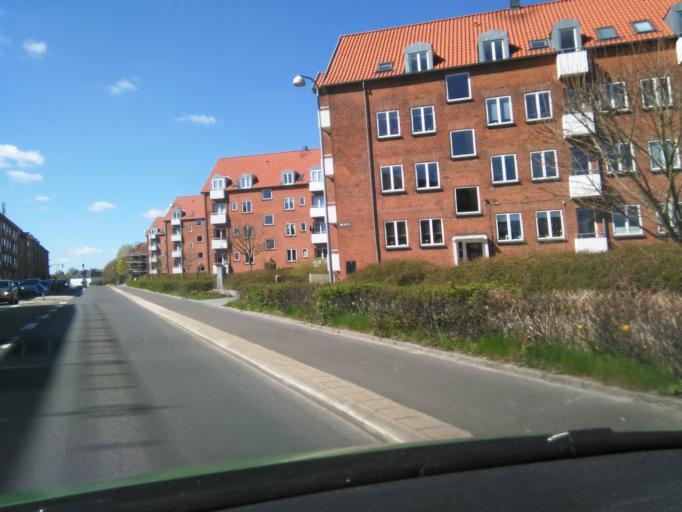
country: DK
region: Central Jutland
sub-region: Horsens Kommune
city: Horsens
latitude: 55.8557
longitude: 9.8357
